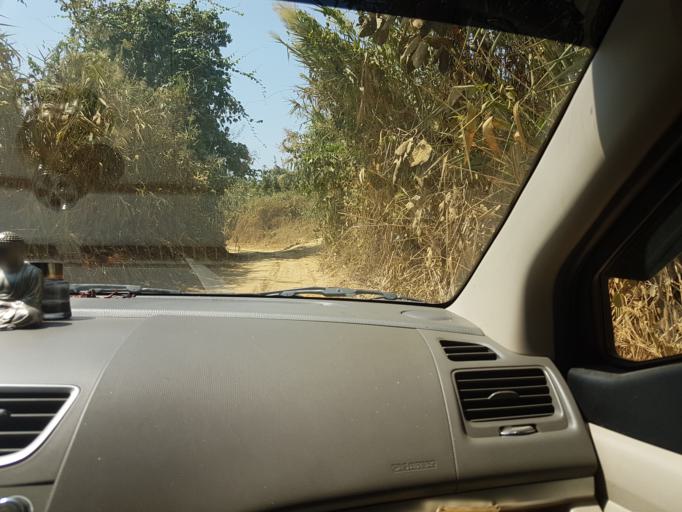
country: MM
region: Bago
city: Pyu
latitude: 18.3825
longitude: 96.4139
